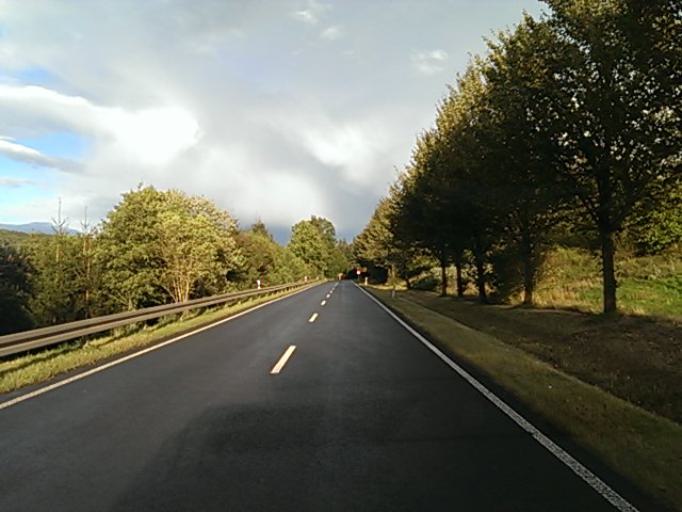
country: DE
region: Thuringia
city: Ostramondra
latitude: 51.1952
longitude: 11.3560
